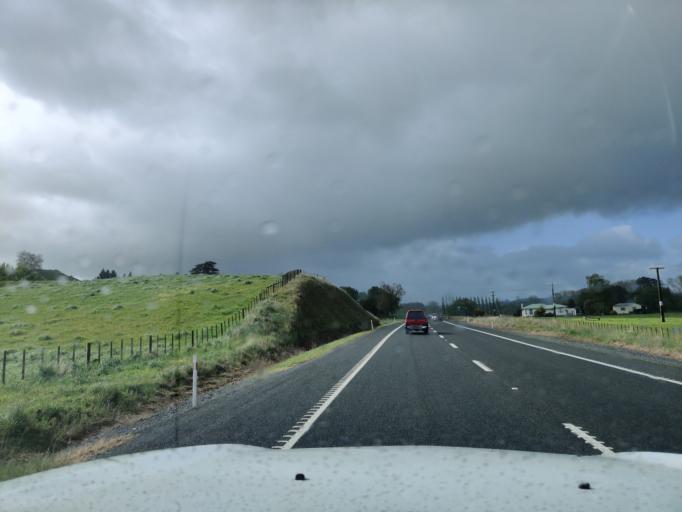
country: NZ
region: Waikato
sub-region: Matamata-Piako District
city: Matamata
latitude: -37.9613
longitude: 175.6872
